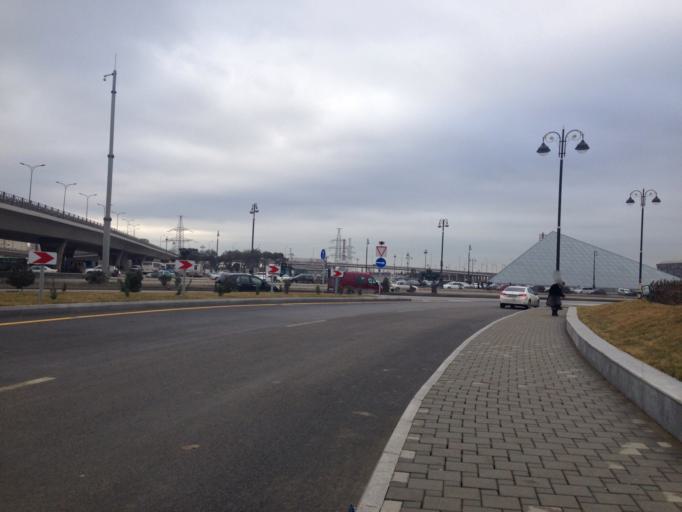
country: AZ
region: Baki
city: Sabuncu
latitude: 40.4224
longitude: 49.9180
